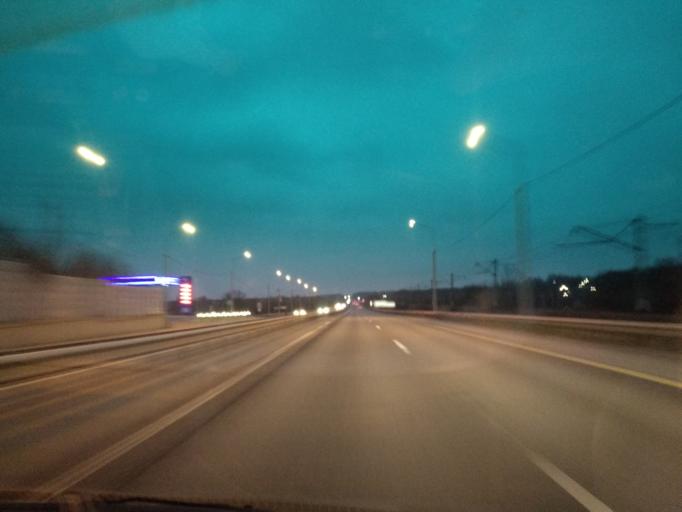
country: RU
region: Adygeya
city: Adygeysk
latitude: 44.8032
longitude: 39.2303
